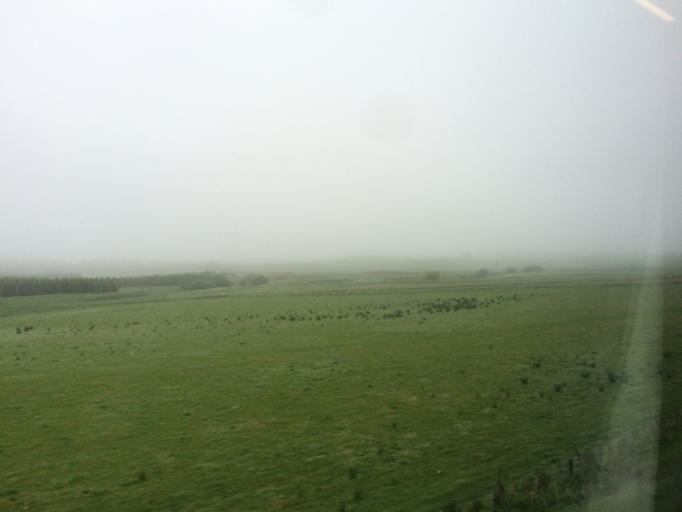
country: GB
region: Scotland
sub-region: Stirling
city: Dunblane
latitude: 56.2250
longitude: -3.9413
